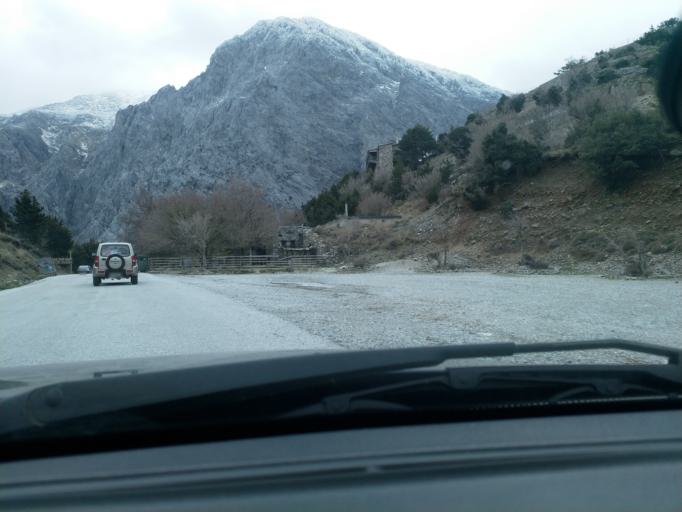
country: GR
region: Crete
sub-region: Nomos Chanias
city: Perivolia
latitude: 35.3091
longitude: 23.9179
